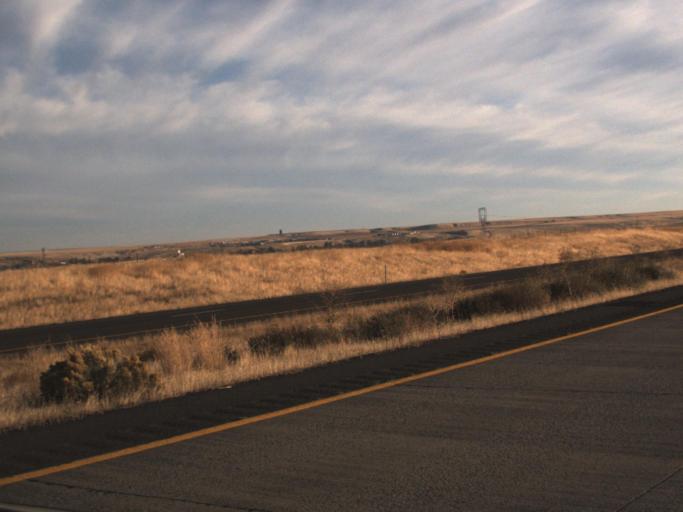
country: US
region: Washington
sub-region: Franklin County
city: Connell
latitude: 46.6363
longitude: -118.8701
